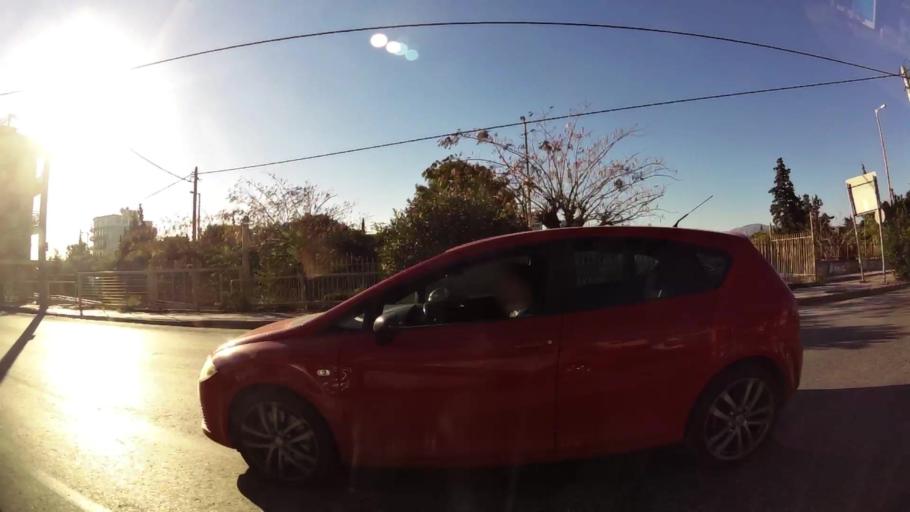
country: GR
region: Attica
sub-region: Nomarchia Athinas
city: Kifisia
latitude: 38.0663
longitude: 23.8098
